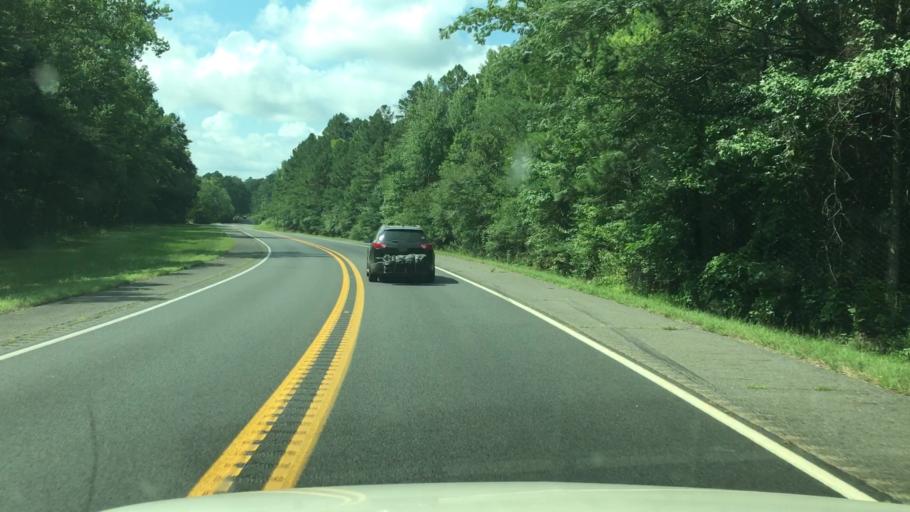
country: US
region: Arkansas
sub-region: Garland County
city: Lake Hamilton
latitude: 34.3522
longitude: -93.1842
